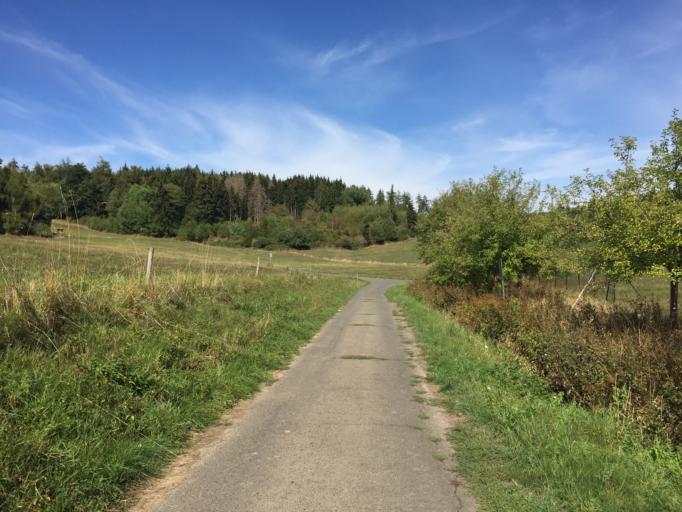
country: DE
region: Hesse
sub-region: Regierungsbezirk Giessen
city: Grunberg
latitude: 50.6042
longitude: 8.8979
